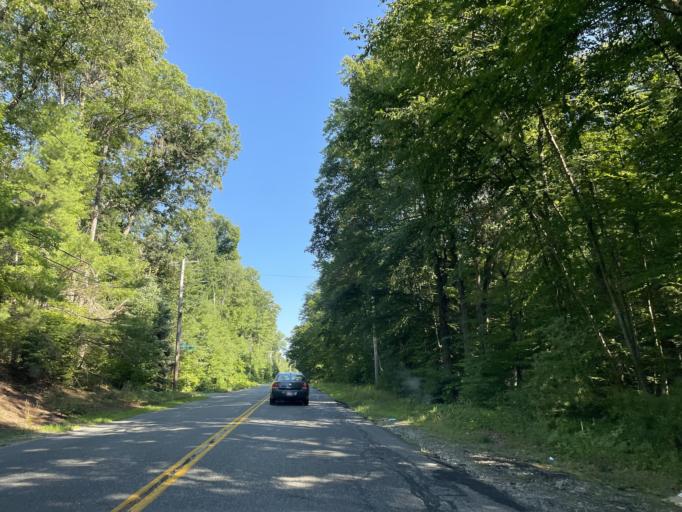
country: US
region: Massachusetts
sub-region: Worcester County
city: East Douglas
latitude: 42.0678
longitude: -71.6976
